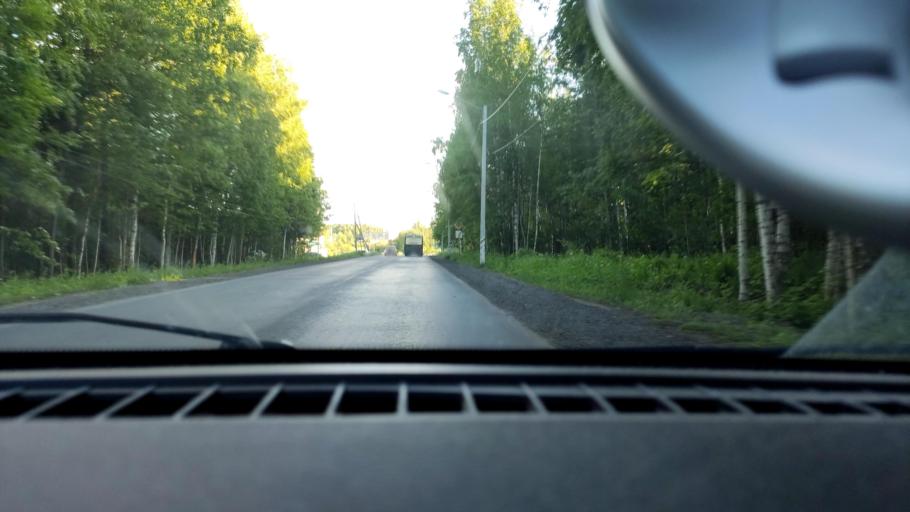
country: RU
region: Perm
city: Perm
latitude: 58.1292
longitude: 56.2986
